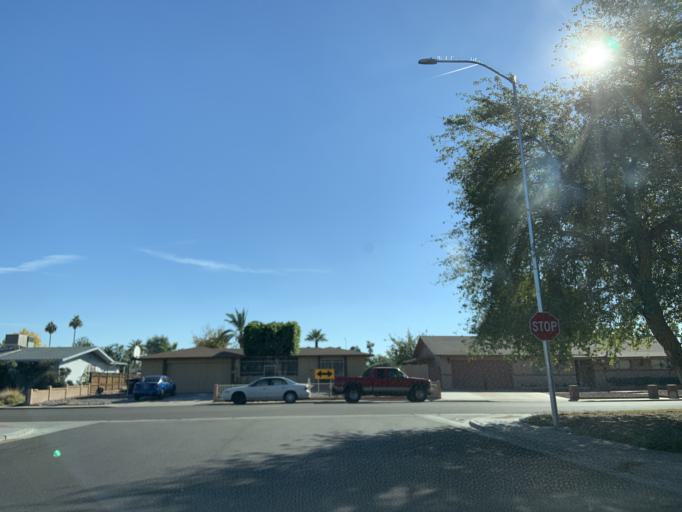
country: US
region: Arizona
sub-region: Maricopa County
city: Tempe
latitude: 33.4038
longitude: -111.8811
